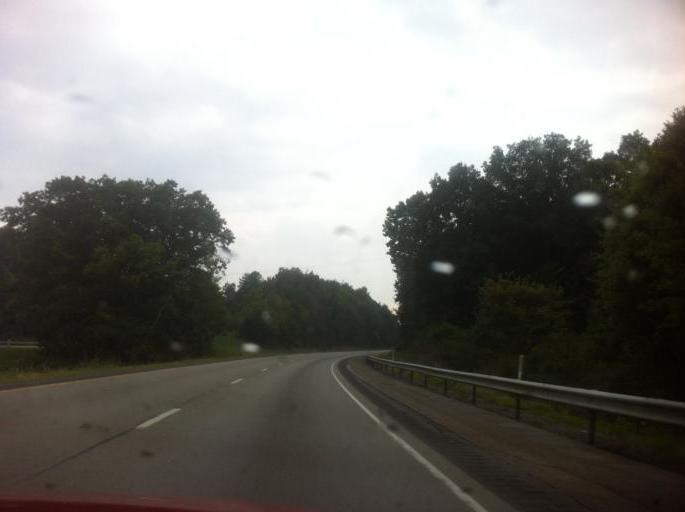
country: US
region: Pennsylvania
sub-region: Clarion County
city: Clarion
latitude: 41.1771
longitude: -79.2512
